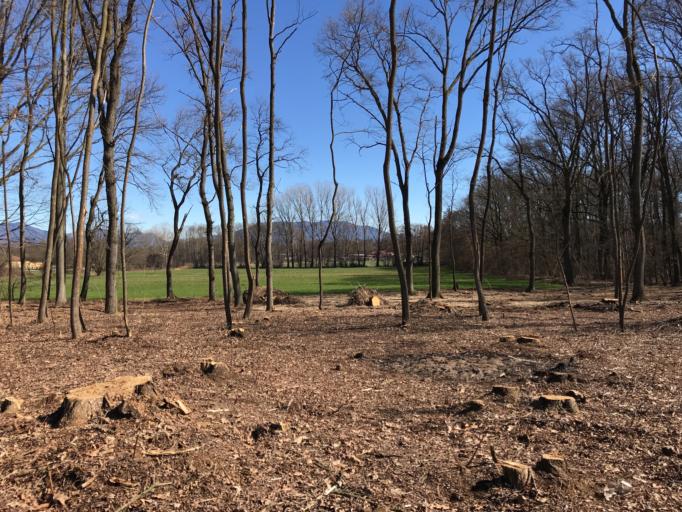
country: IT
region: Lombardy
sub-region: Provincia di Varese
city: Angera
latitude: 45.7793
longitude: 8.6006
